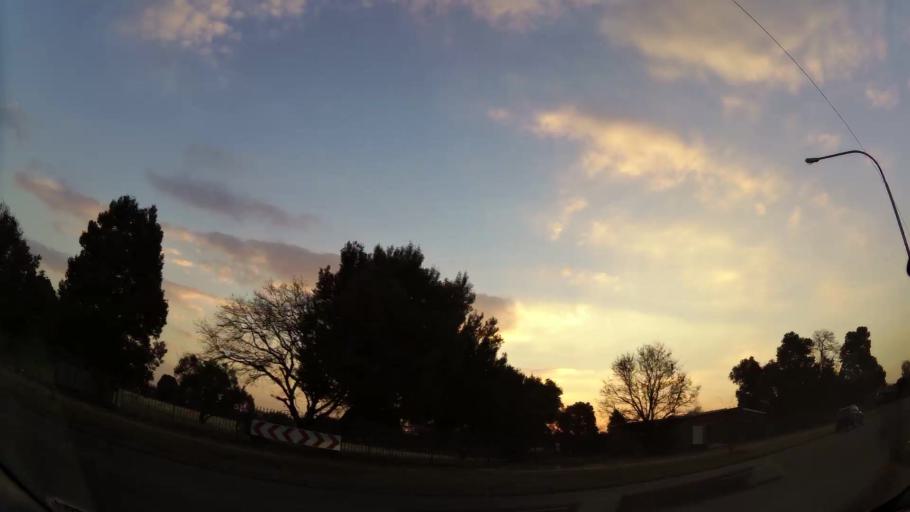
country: ZA
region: Gauteng
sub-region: Ekurhuleni Metropolitan Municipality
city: Benoni
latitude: -26.1727
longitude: 28.3184
